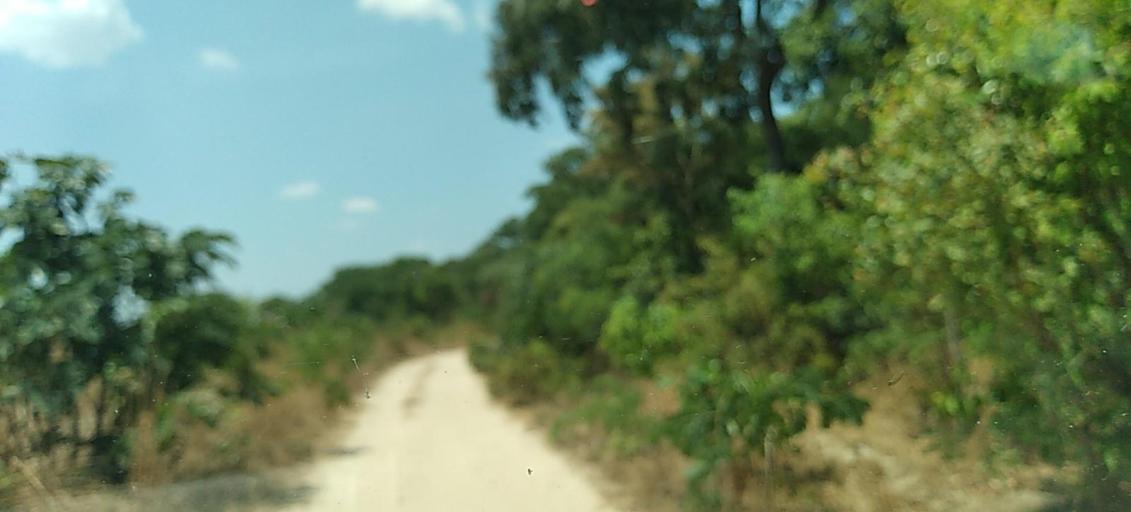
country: ZM
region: Central
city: Kapiri Mposhi
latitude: -13.6618
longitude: 28.4912
